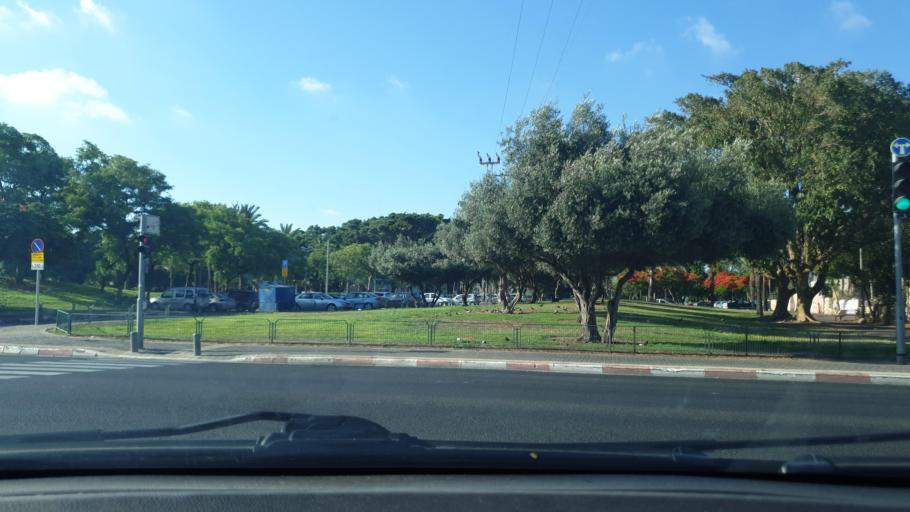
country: IL
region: Tel Aviv
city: Giv`atayim
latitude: 32.0564
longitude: 34.8065
